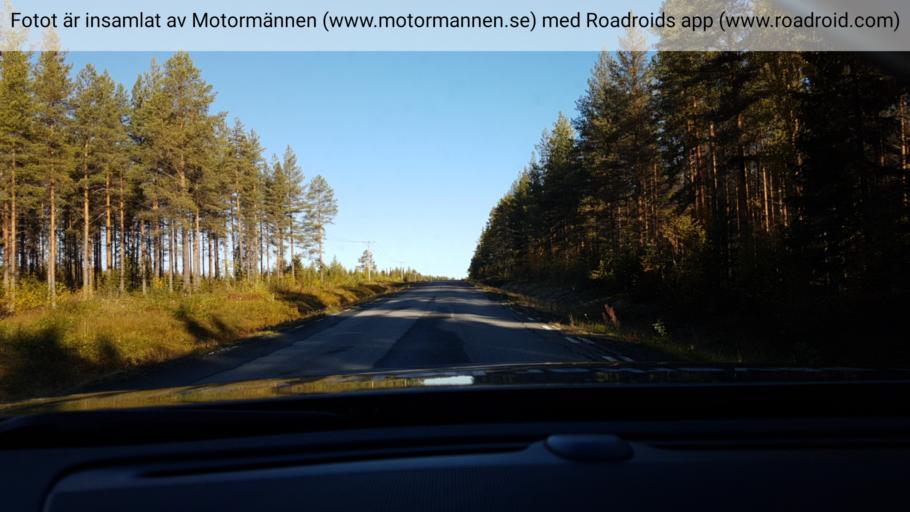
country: SE
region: Norrbotten
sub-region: Bodens Kommun
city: Boden
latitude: 65.9412
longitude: 21.6392
